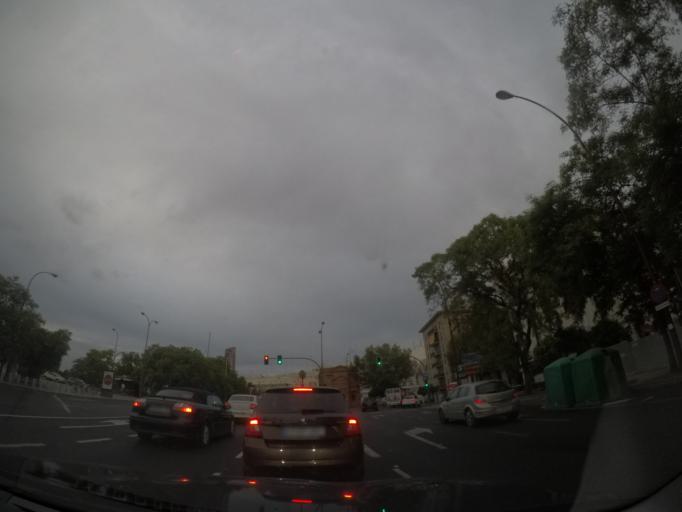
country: ES
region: Andalusia
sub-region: Provincia de Sevilla
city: Sevilla
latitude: 37.3871
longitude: -6.0010
